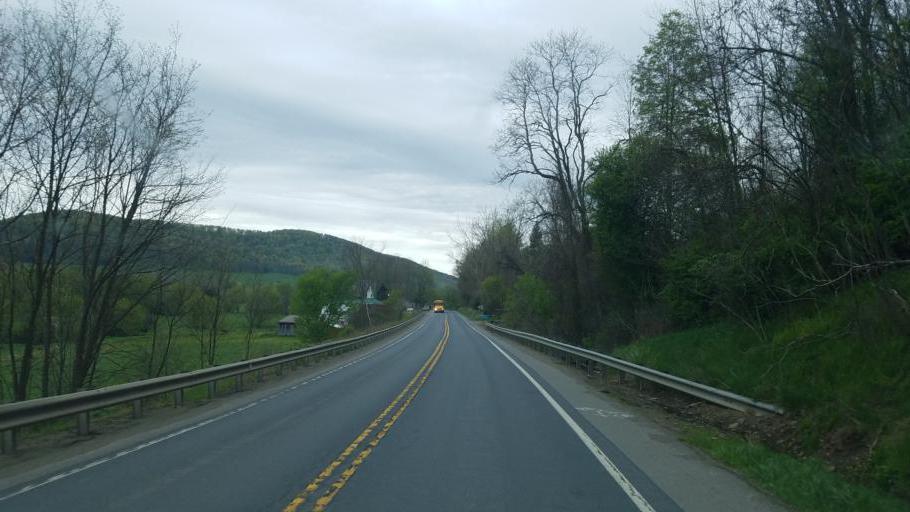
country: US
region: Pennsylvania
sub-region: Tioga County
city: Westfield
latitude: 41.9423
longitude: -77.4780
